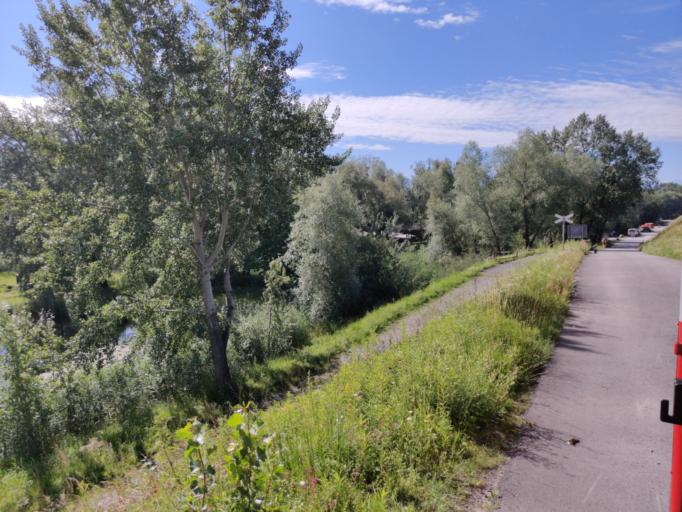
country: AT
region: Vorarlberg
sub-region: Politischer Bezirk Bregenz
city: Hard
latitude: 47.4895
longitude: 9.6719
